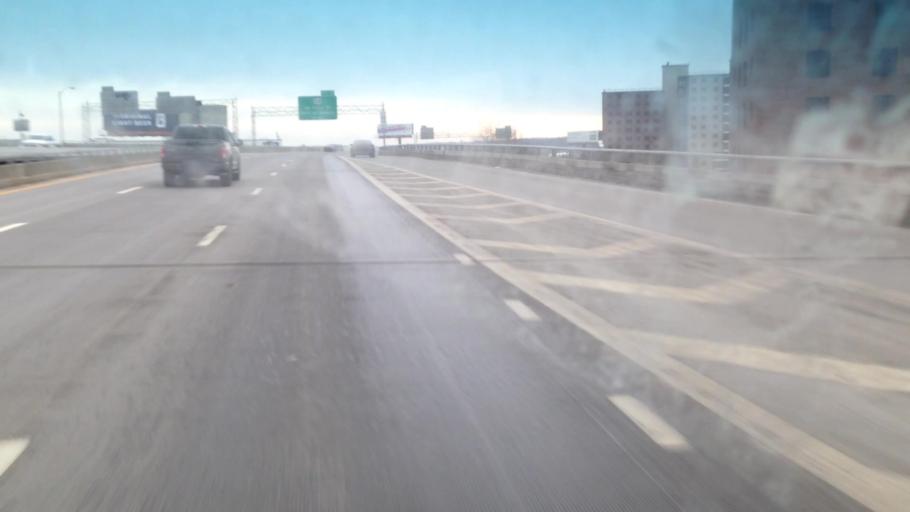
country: US
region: New York
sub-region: Rensselaer County
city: Rensselaer
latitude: 42.6411
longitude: -73.7526
